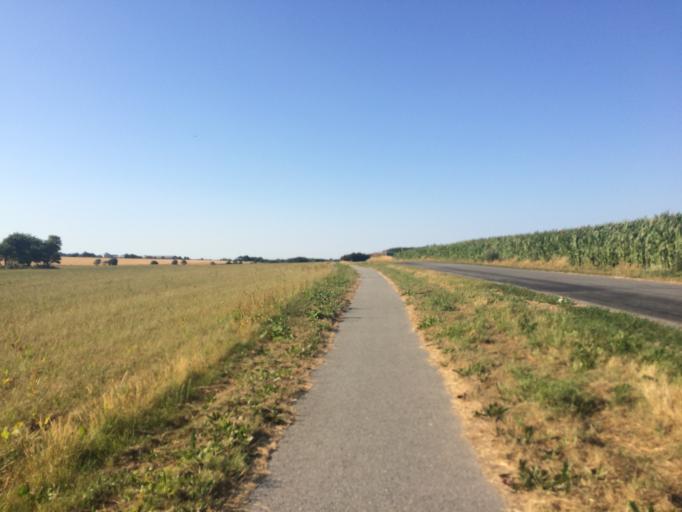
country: DK
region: Central Jutland
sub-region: Holstebro Kommune
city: Vinderup
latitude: 56.6021
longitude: 8.7716
